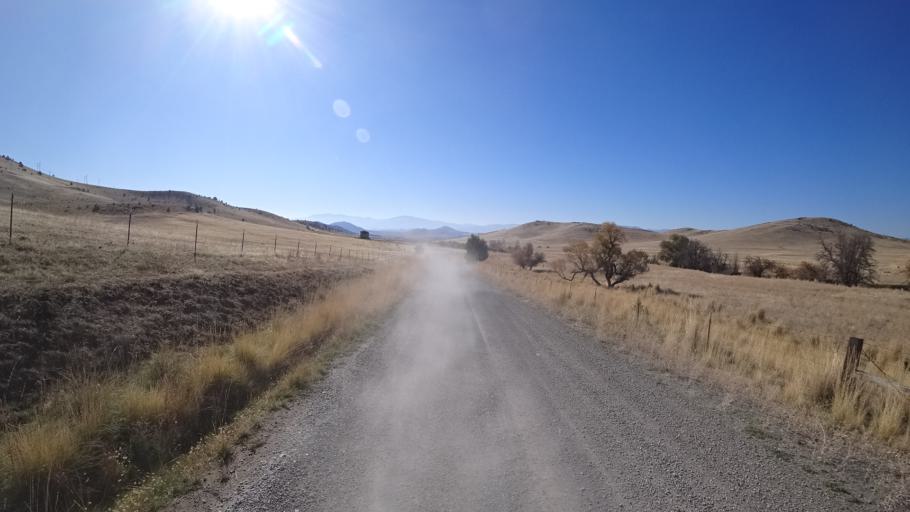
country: US
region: California
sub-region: Siskiyou County
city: Montague
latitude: 41.7470
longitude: -122.3629
